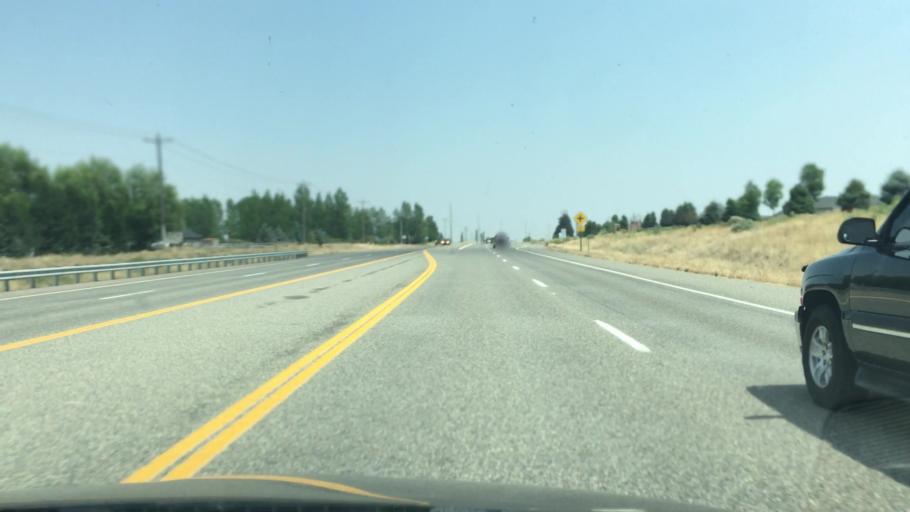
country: US
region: Idaho
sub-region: Twin Falls County
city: Twin Falls
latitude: 42.5935
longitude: -114.5280
